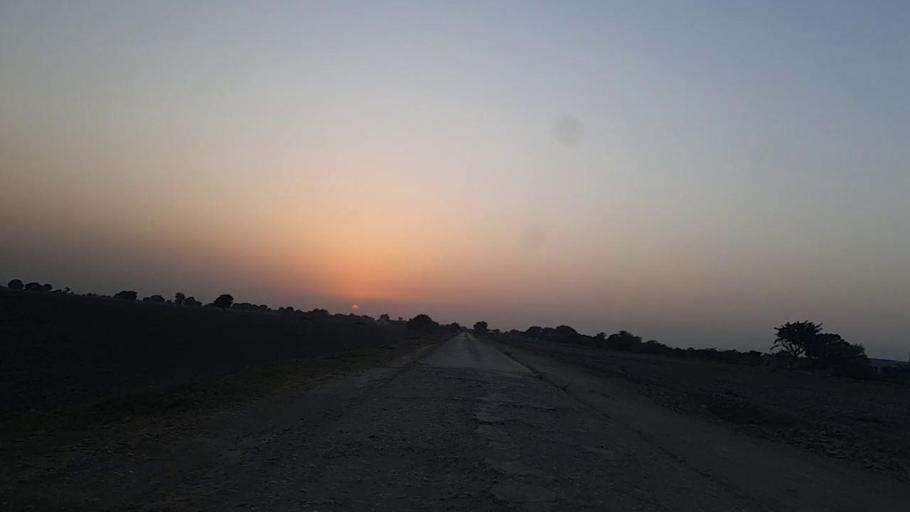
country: PK
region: Sindh
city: Naukot
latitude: 24.7483
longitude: 69.3227
